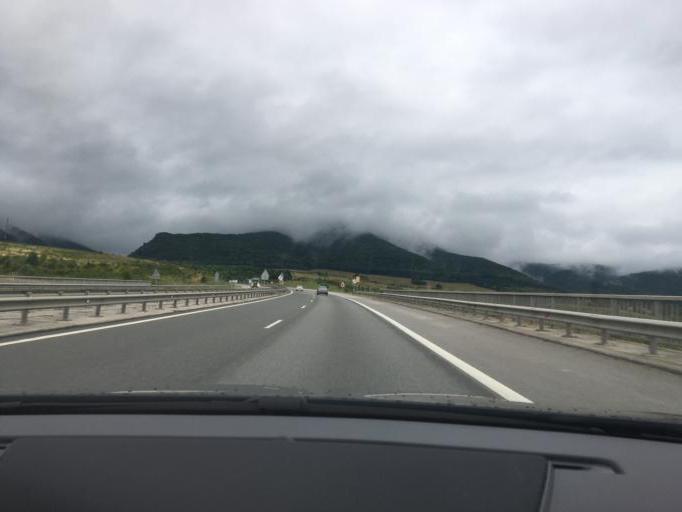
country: BG
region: Sofiya
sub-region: Obshtina Bozhurishte
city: Bozhurishte
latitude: 42.6881
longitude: 23.1567
